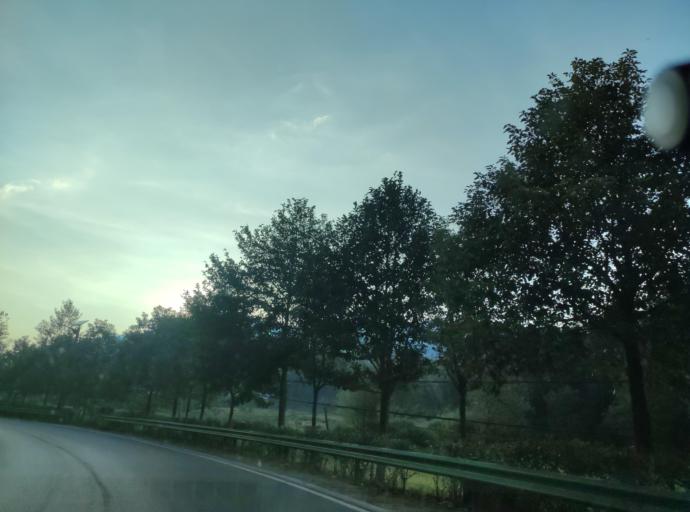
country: CN
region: Jiangxi Sheng
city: Zhangjiafang
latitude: 27.5283
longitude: 114.0257
